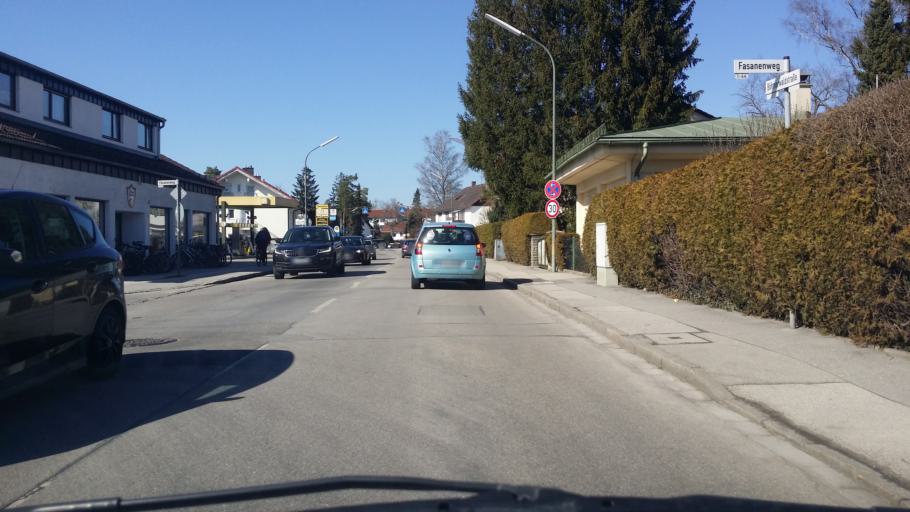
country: DE
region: Bavaria
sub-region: Upper Bavaria
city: Geretsried
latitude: 47.8759
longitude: 11.4708
